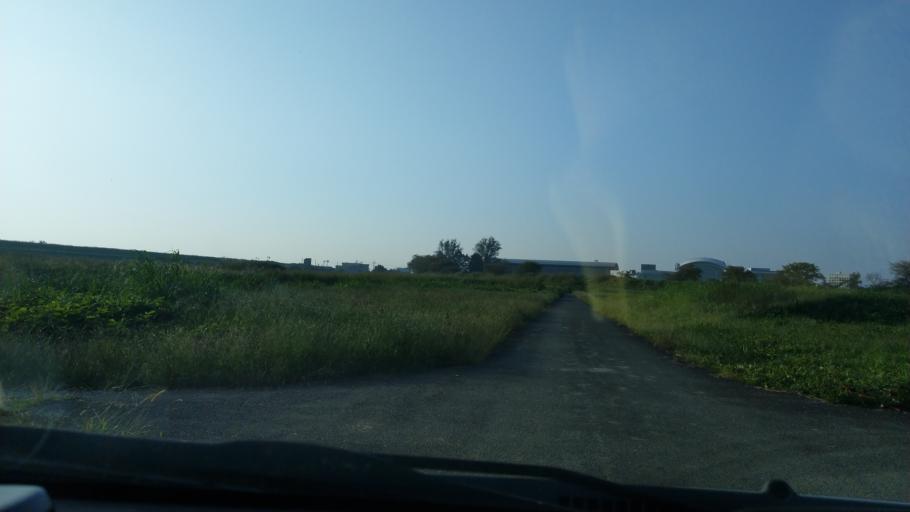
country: JP
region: Saitama
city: Shiki
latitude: 35.8517
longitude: 139.6135
